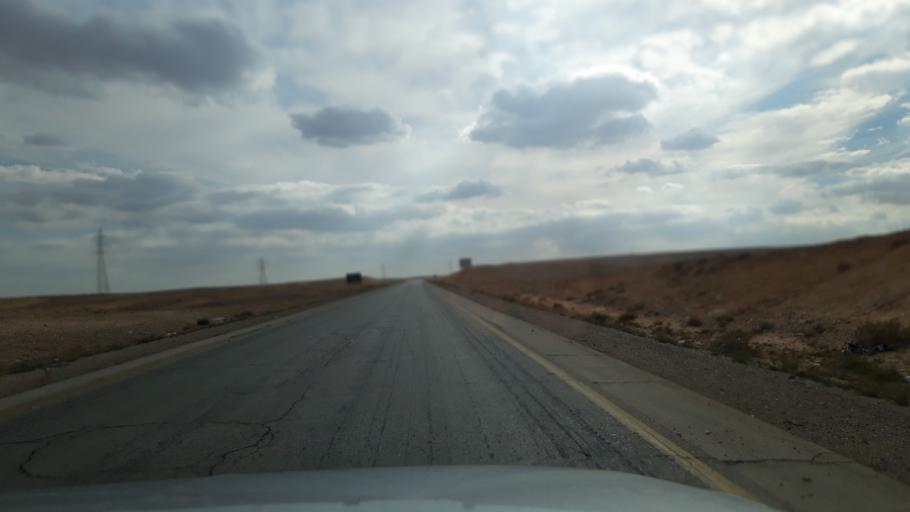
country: JO
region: Amman
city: Al Azraq ash Shamali
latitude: 31.7472
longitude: 36.5388
